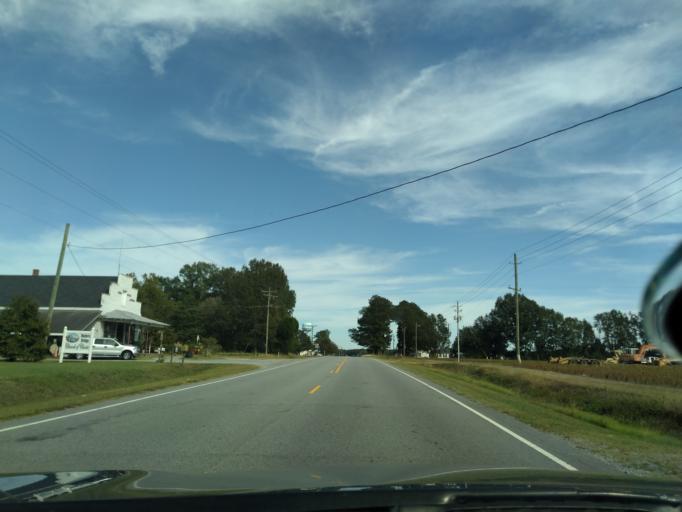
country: US
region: North Carolina
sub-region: Beaufort County
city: River Road
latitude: 35.5231
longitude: -76.8077
